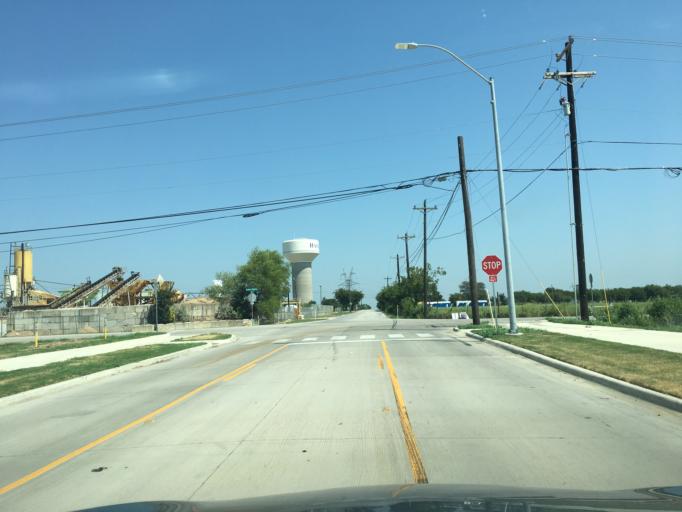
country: US
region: Texas
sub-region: Tarrant County
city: Haslet
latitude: 32.9416
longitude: -97.3190
